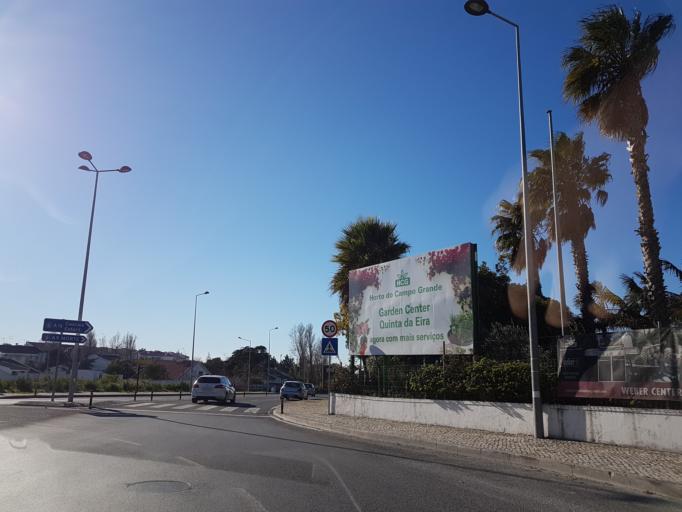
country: PT
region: Lisbon
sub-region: Sintra
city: Sintra
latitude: 38.7734
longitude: -9.3812
